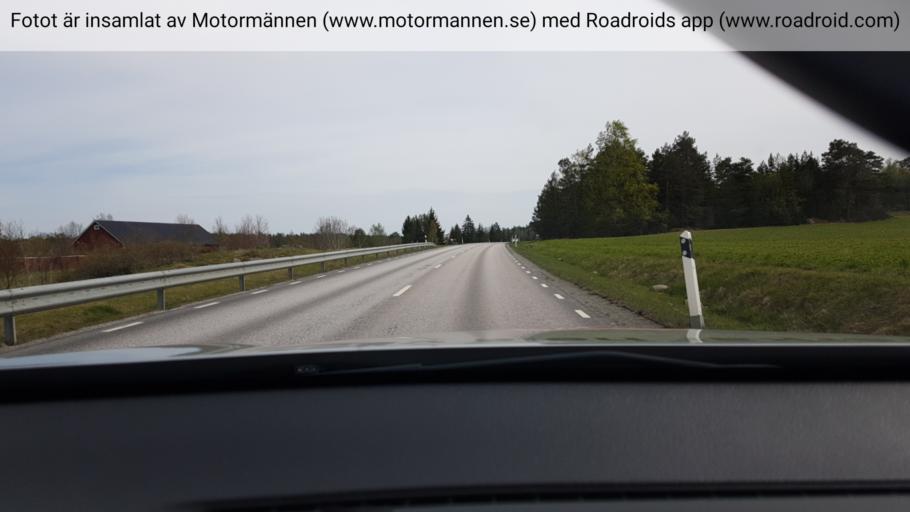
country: SE
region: Stockholm
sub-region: Vallentuna Kommun
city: Vallentuna
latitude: 59.7398
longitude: 18.0546
